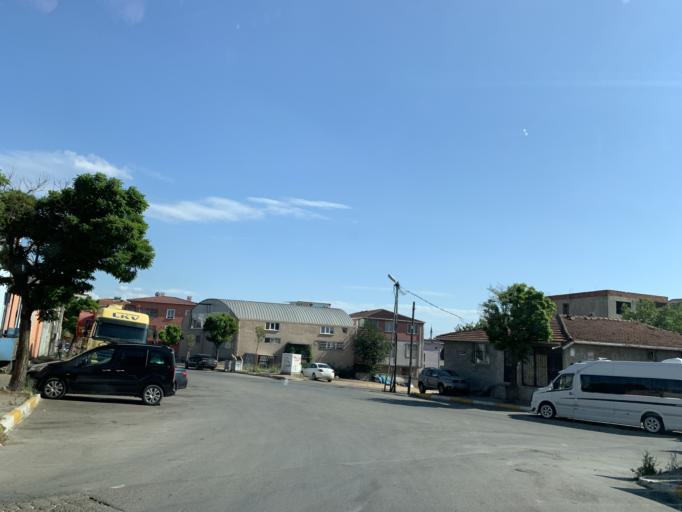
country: TR
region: Istanbul
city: Pendik
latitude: 40.8868
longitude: 29.2778
